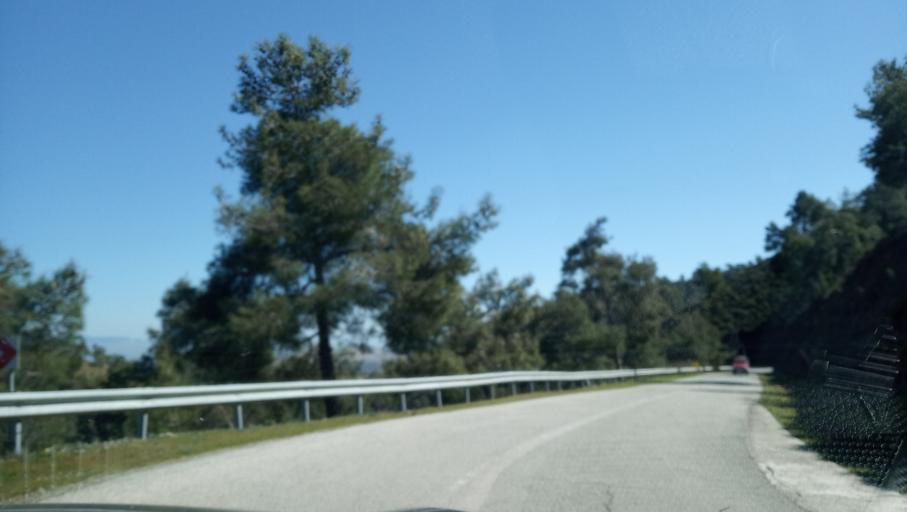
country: CY
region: Lefkosia
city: Lefka
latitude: 35.0676
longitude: 32.8172
